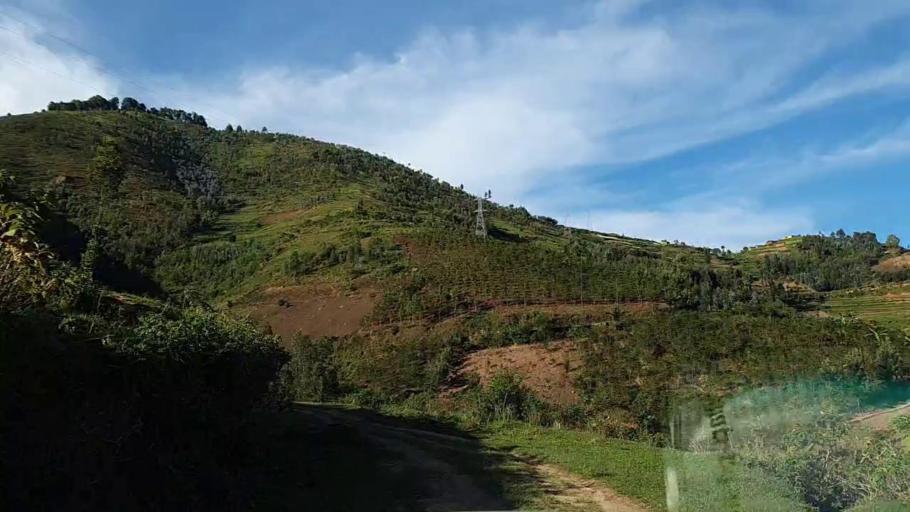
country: RW
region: Southern Province
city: Nzega
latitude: -2.4174
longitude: 29.5142
